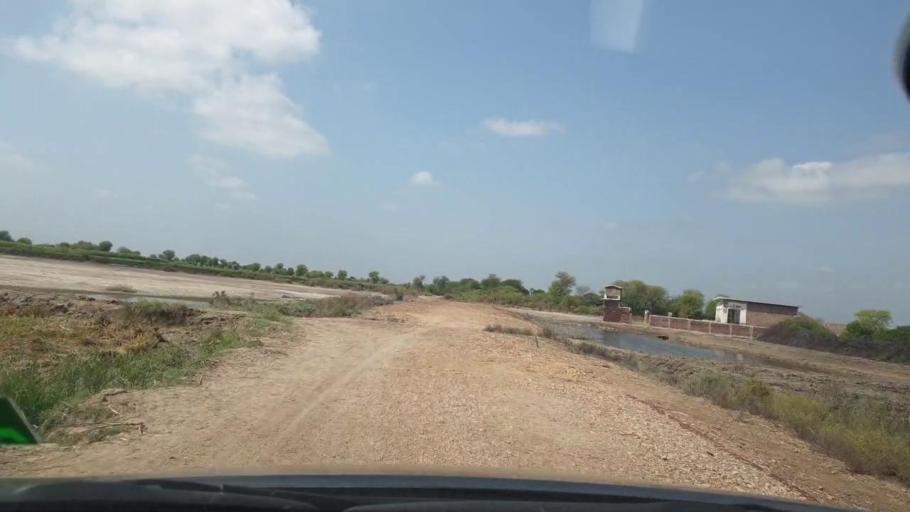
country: PK
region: Sindh
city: Tando Bago
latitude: 24.8351
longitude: 69.0444
